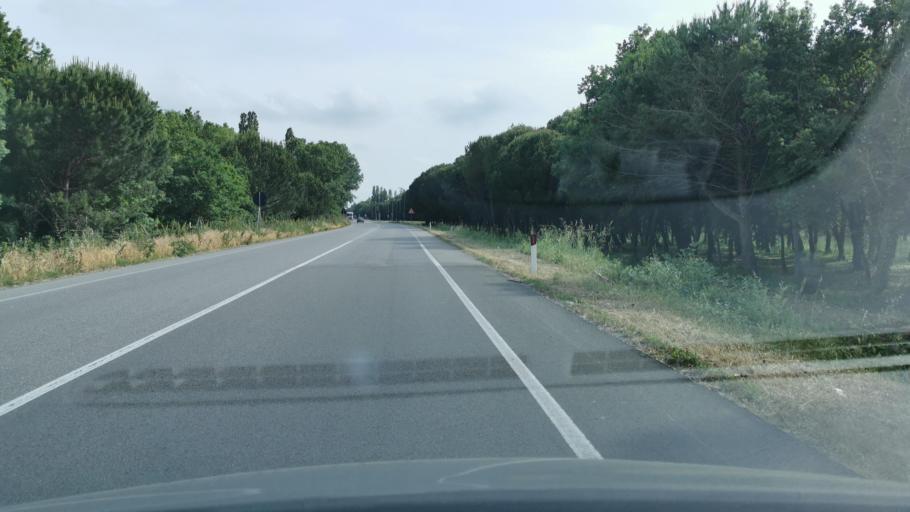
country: IT
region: Emilia-Romagna
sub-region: Provincia di Ravenna
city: Marina Romea
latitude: 44.4824
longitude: 12.2116
